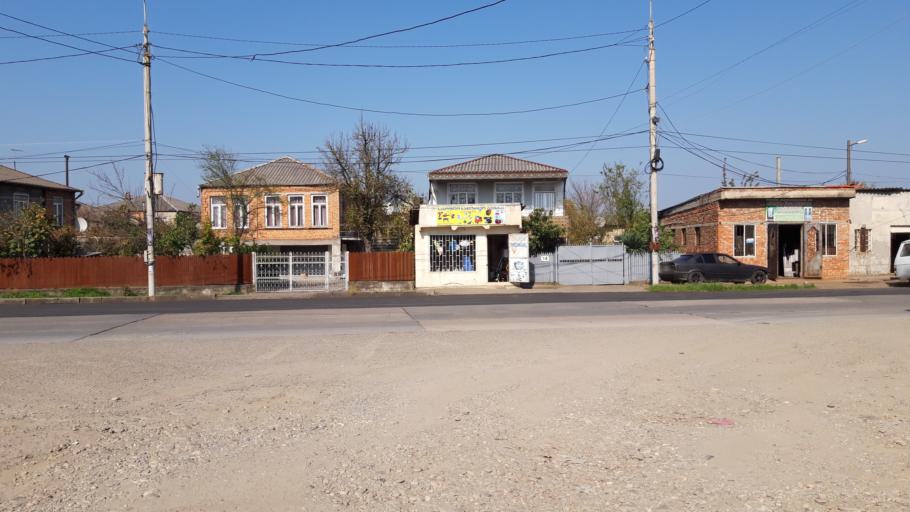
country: GE
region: Imereti
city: Samtredia
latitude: 42.1602
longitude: 42.3376
